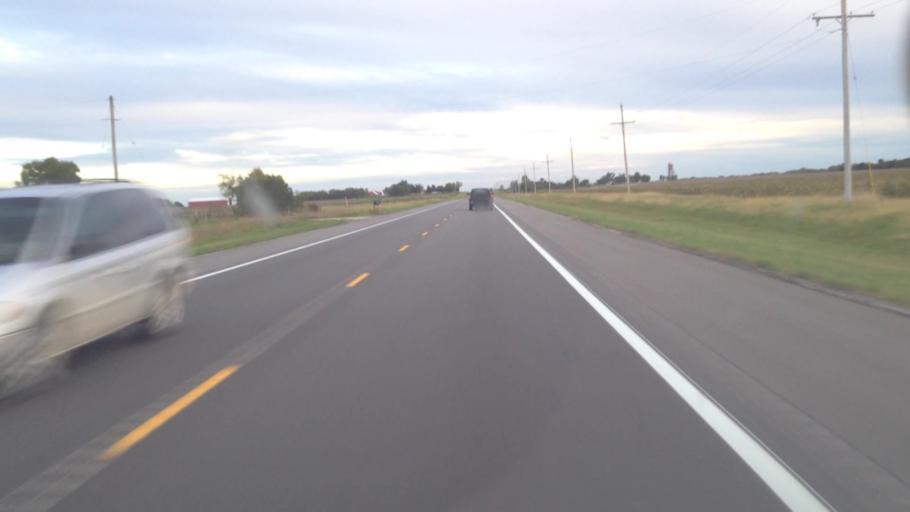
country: US
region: Kansas
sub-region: Franklin County
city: Ottawa
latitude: 38.5188
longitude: -95.2676
